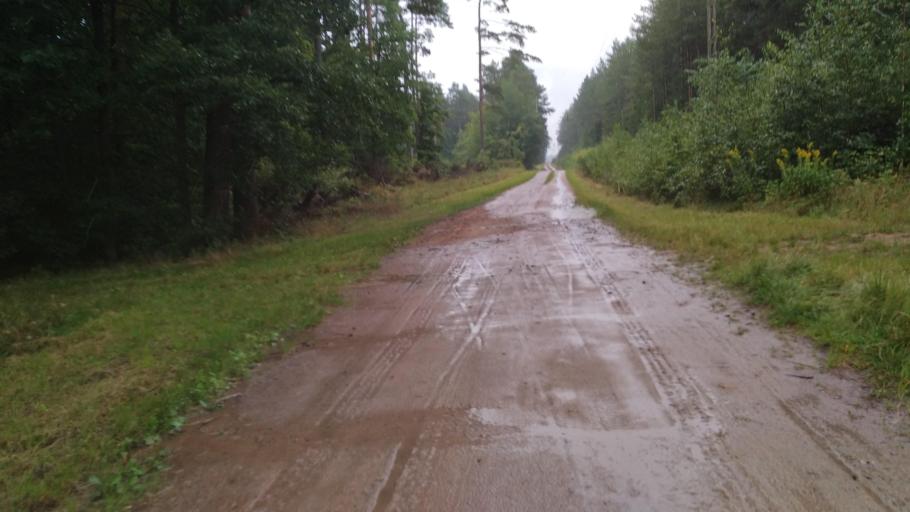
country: PL
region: Pomeranian Voivodeship
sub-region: Powiat wejherowski
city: Goscicino
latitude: 54.6216
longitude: 18.1505
